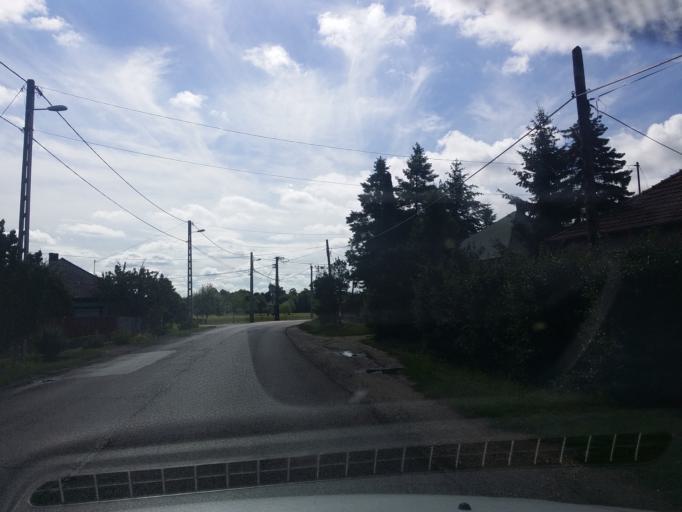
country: HU
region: Jasz-Nagykun-Szolnok
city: Jaszszentandras
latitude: 47.6423
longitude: 20.1923
